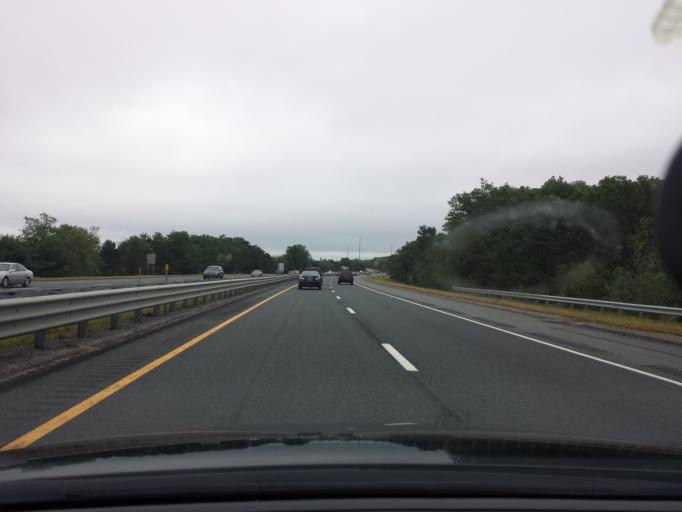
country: US
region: Rhode Island
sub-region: Kent County
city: West Warwick
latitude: 41.6584
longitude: -71.5592
